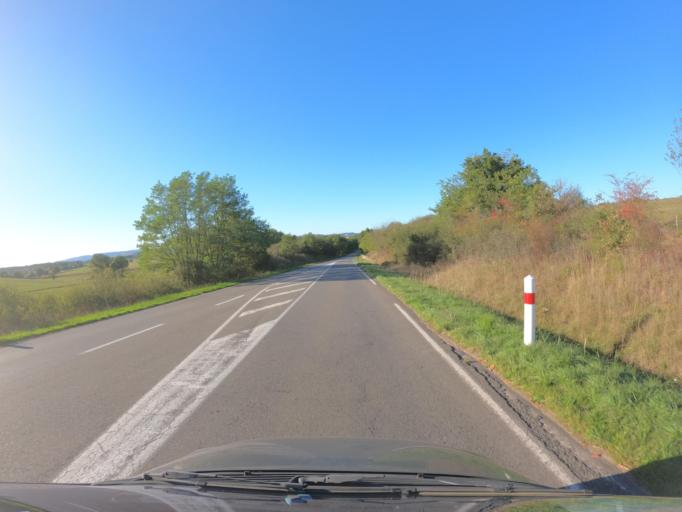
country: FR
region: Bourgogne
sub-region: Departement de Saone-et-Loire
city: Torcy
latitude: 46.7459
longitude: 4.4432
